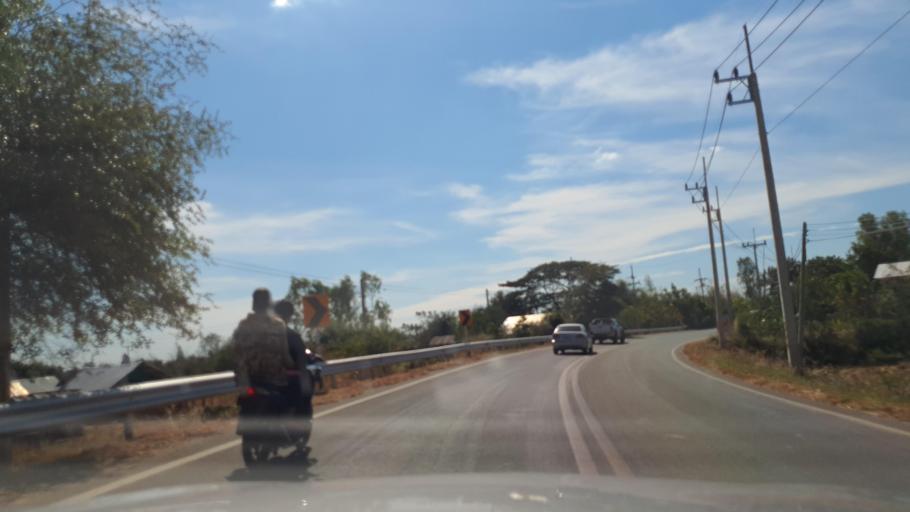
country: TH
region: Kalasin
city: Khao Wong
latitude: 16.7482
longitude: 104.1168
